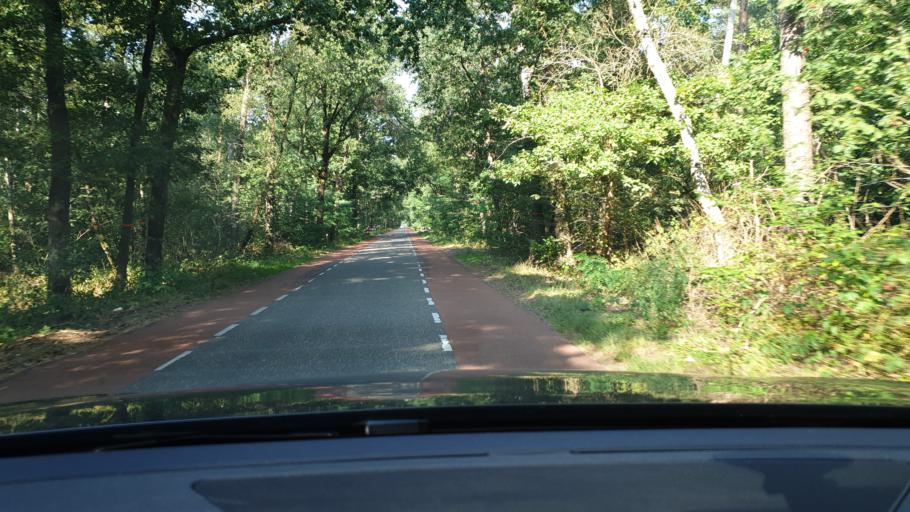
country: NL
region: North Brabant
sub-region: Gemeente Bernheze
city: Loosbroek
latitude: 51.6651
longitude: 5.4617
